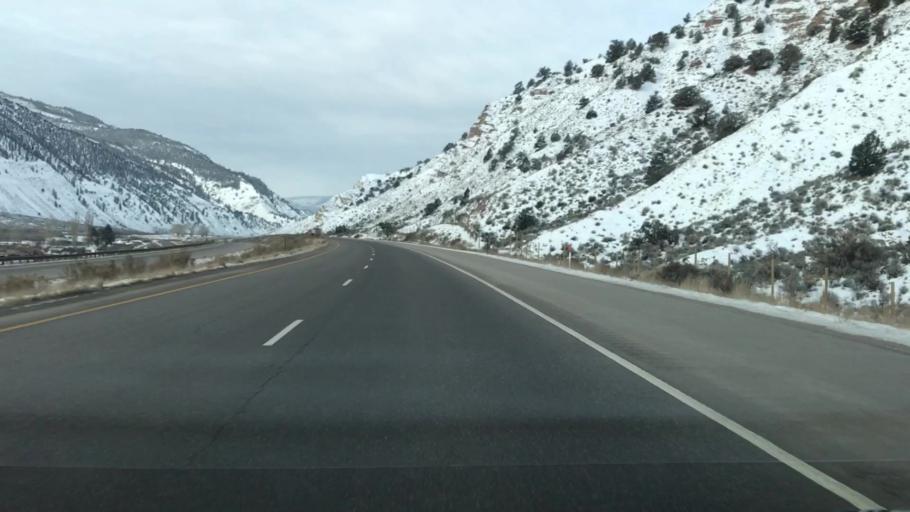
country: US
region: Colorado
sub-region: Eagle County
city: Gypsum
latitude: 39.6486
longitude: -107.0112
